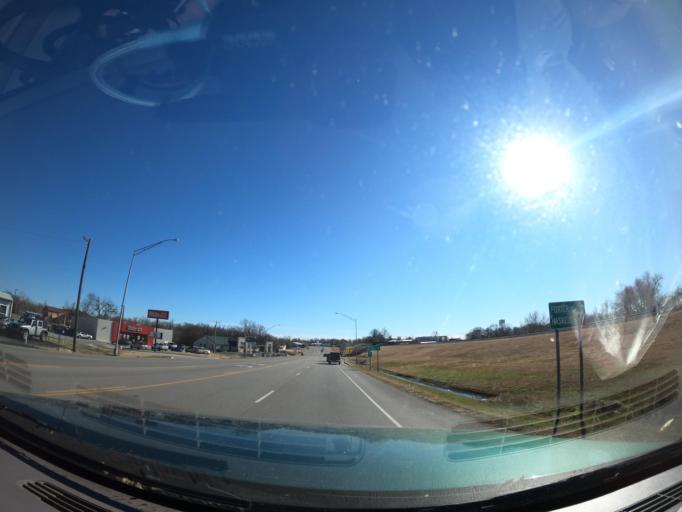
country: US
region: Oklahoma
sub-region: Wagoner County
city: Coweta
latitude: 35.9577
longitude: -95.6508
